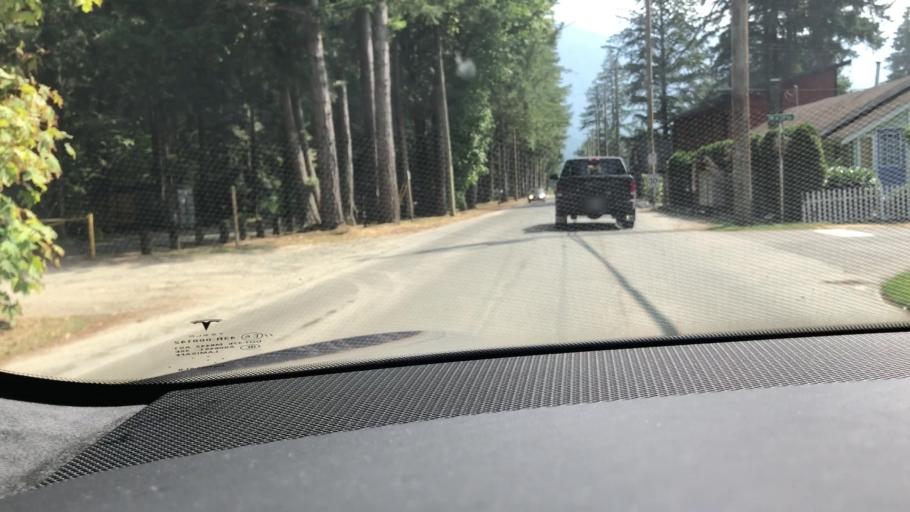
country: CA
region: British Columbia
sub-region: Fraser Valley Regional District
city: Chilliwack
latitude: 49.0714
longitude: -121.9763
